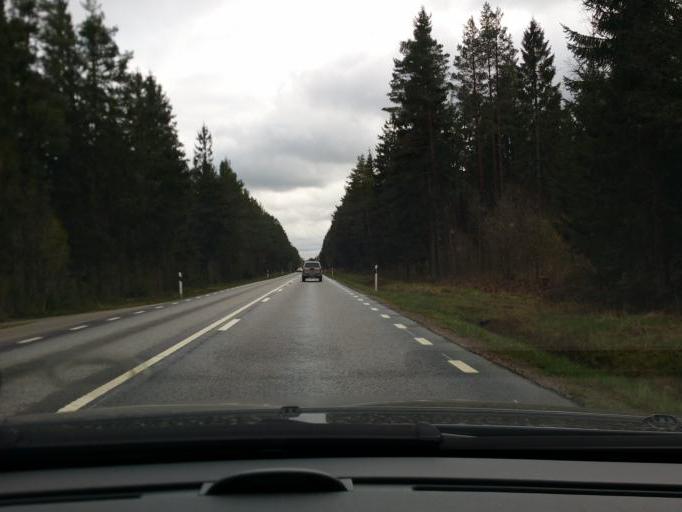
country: SE
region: Kronoberg
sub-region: Vaxjo Kommun
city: Ingelstad
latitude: 56.7970
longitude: 14.8936
